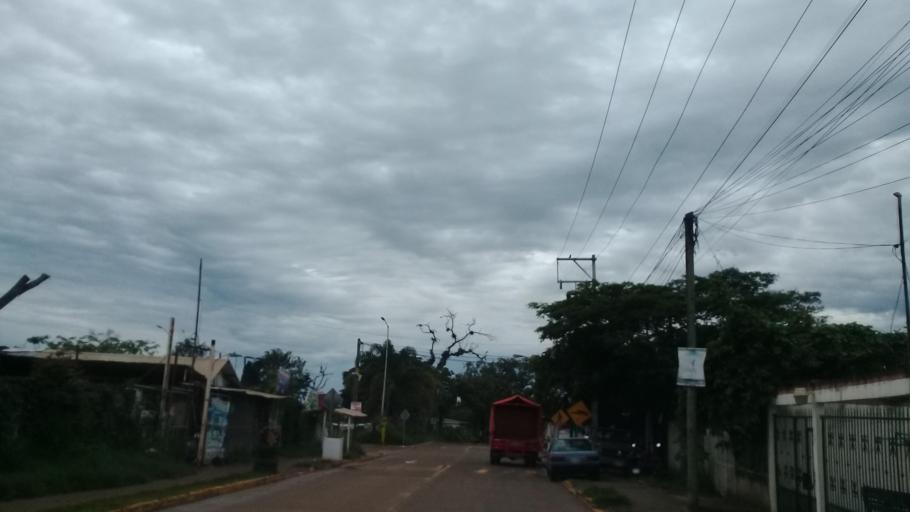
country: MX
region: Veracruz
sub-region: Emiliano Zapata
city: Las Trancas
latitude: 19.5036
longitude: -96.8693
